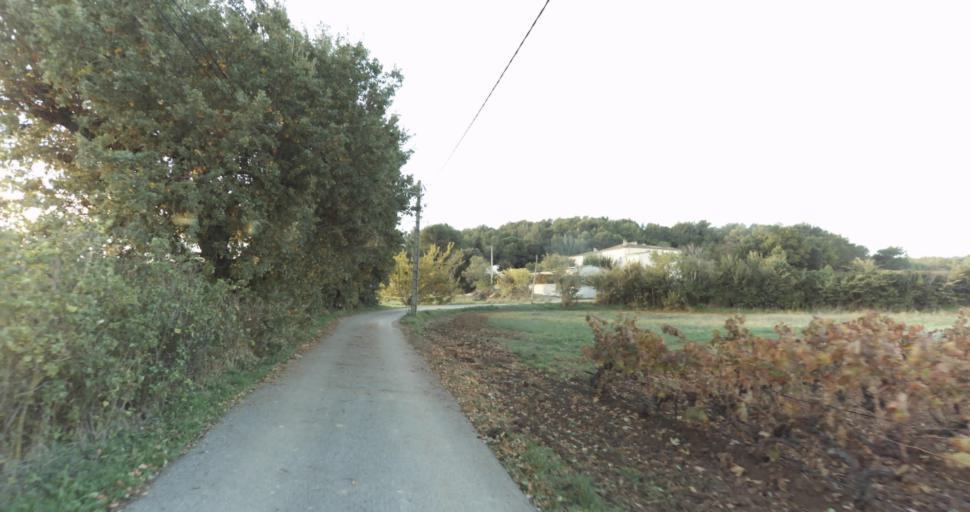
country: FR
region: Provence-Alpes-Cote d'Azur
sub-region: Departement des Bouches-du-Rhone
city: Venelles
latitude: 43.5737
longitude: 5.4938
